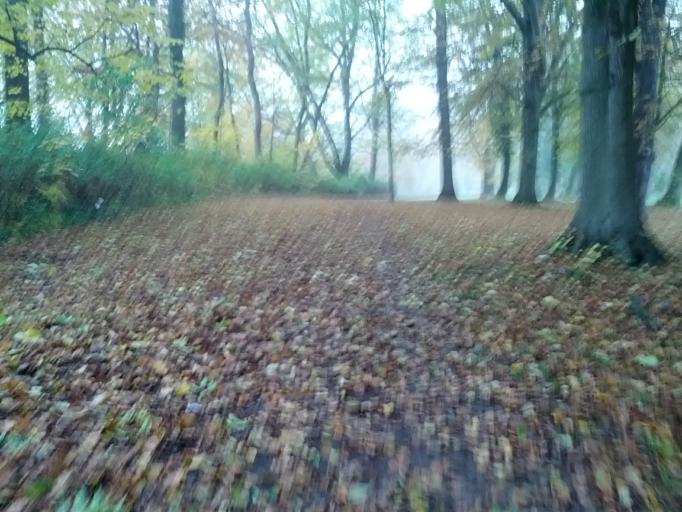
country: DE
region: Thuringia
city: Eisenach
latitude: 50.9883
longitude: 10.3594
